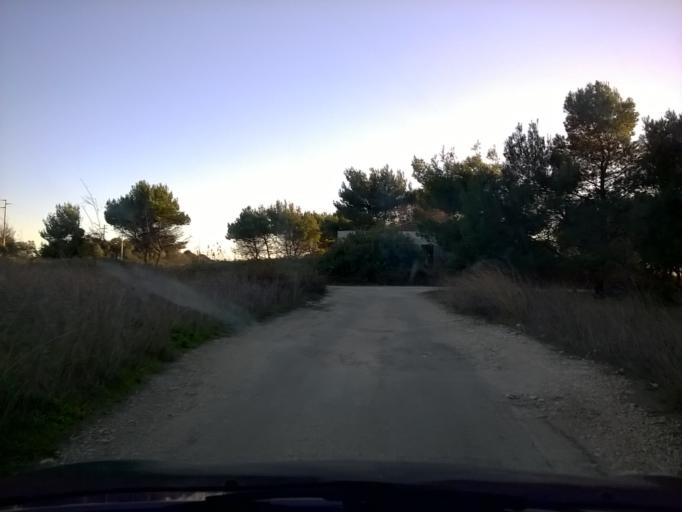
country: IT
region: Apulia
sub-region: Provincia di Taranto
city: Paolo VI
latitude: 40.4949
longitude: 17.2677
